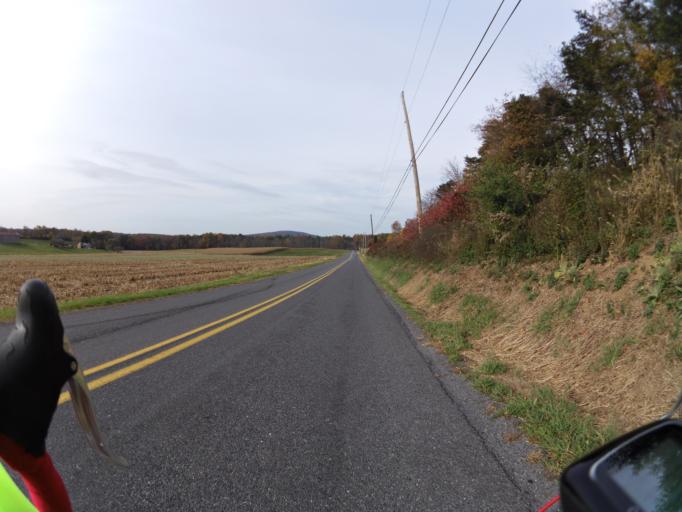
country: US
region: Pennsylvania
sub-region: Union County
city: New Columbia
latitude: 41.0492
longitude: -76.9407
